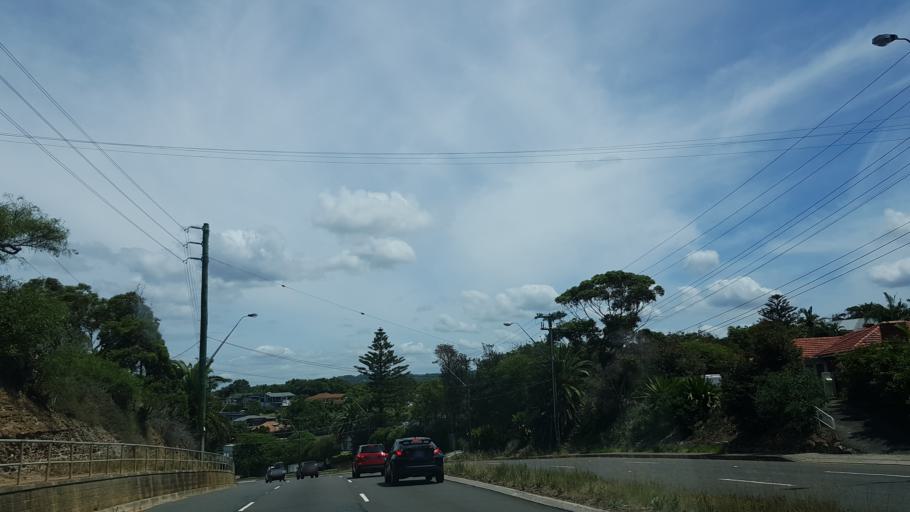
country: AU
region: New South Wales
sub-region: Pittwater
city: Newport
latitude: -33.6702
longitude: 151.3152
